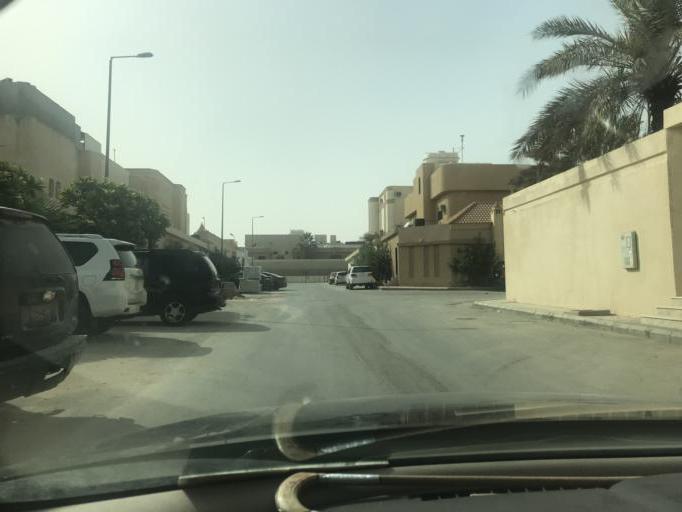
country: SA
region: Ar Riyad
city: Riyadh
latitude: 24.7585
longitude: 46.7679
